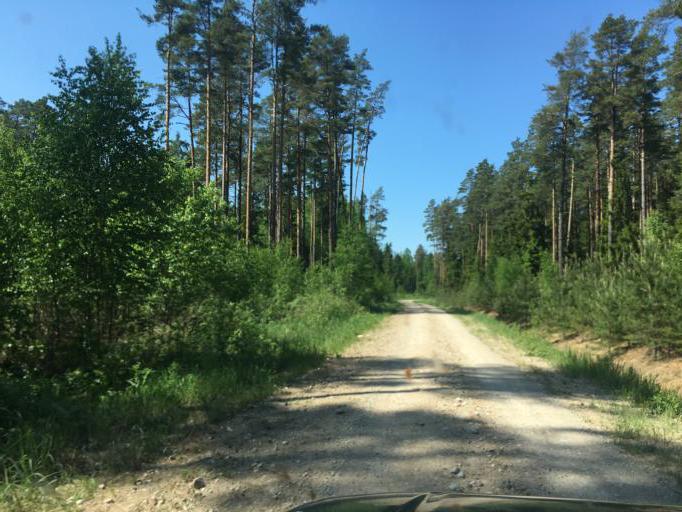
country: LV
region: Talsu Rajons
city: Valdemarpils
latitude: 57.4441
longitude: 22.6616
